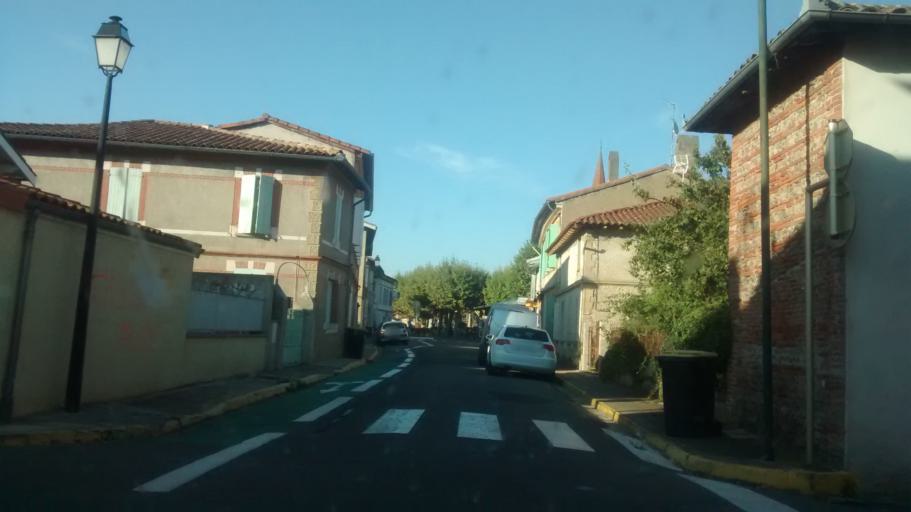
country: FR
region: Midi-Pyrenees
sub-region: Departement de la Haute-Garonne
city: Lherm
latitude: 43.4286
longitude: 1.2222
